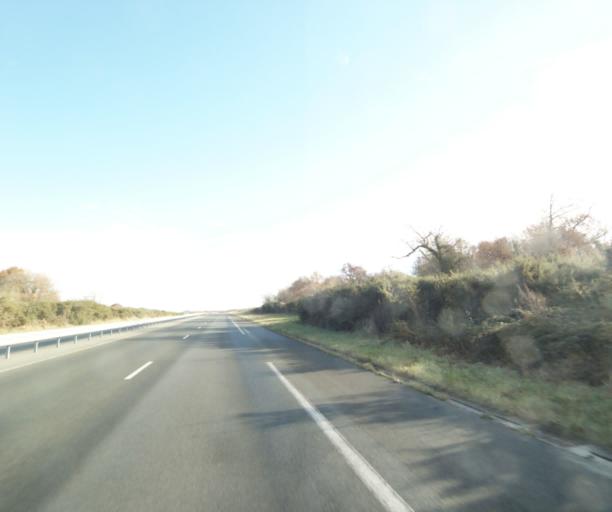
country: FR
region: Poitou-Charentes
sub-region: Departement de la Charente-Maritime
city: Saint-Romain-de-Benet
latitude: 45.6965
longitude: -0.8125
